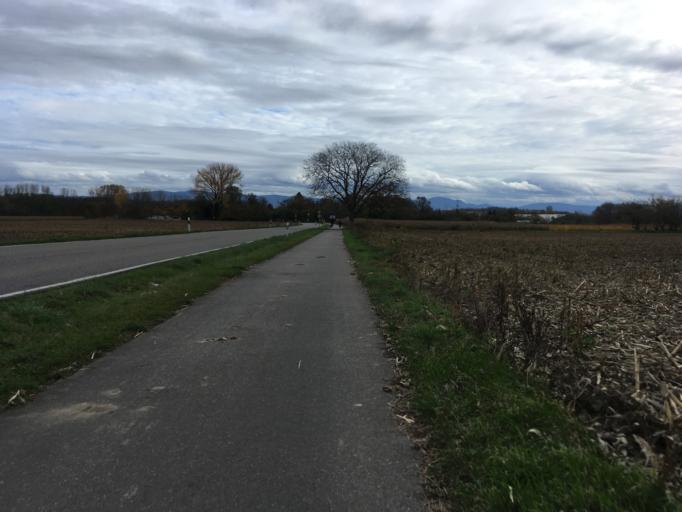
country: DE
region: Baden-Wuerttemberg
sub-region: Freiburg Region
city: Ihringen
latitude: 48.0342
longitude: 7.6533
